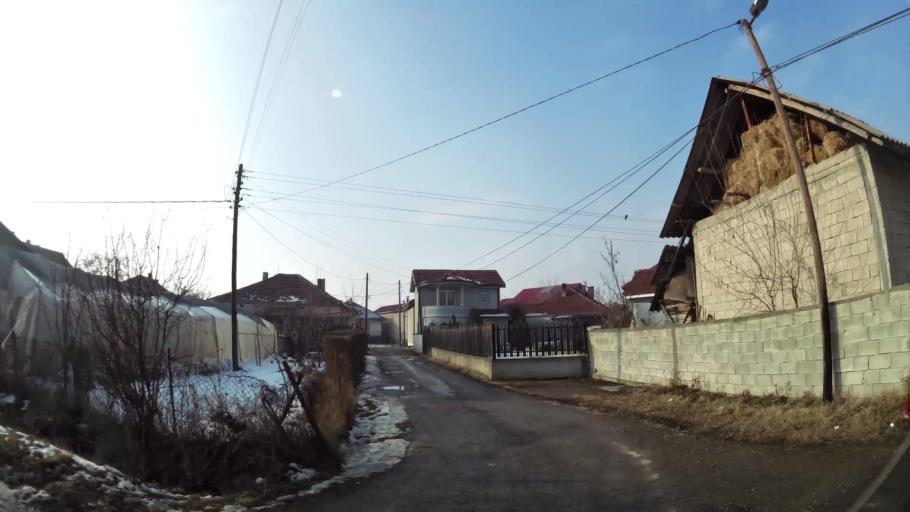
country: MK
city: Kadino
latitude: 41.9676
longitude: 21.6003
